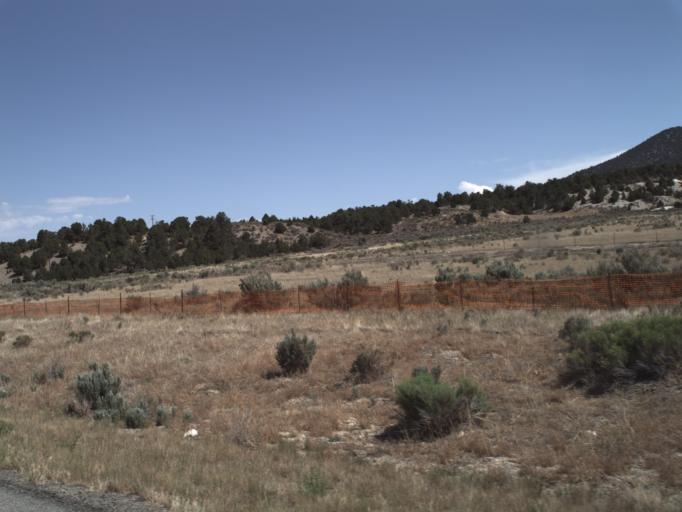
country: US
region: Utah
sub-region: Utah County
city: Genola
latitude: 39.9671
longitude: -112.2534
